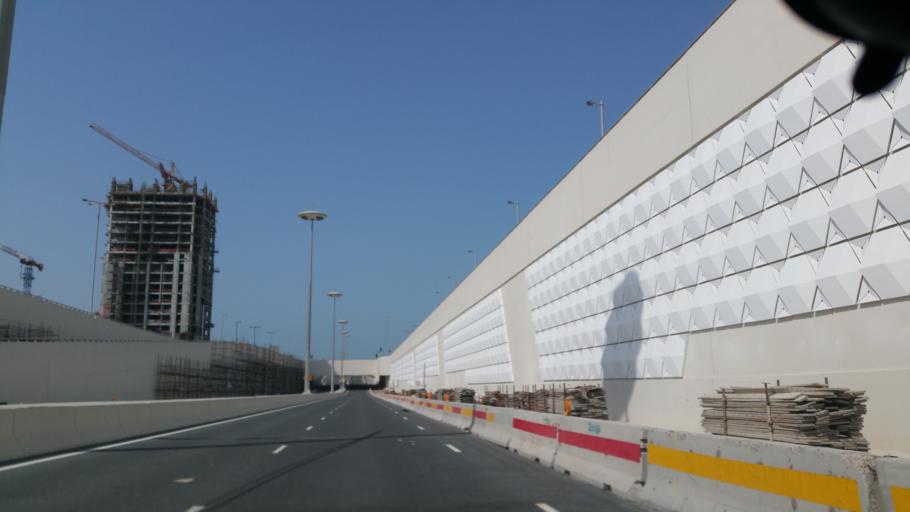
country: QA
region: Baladiyat Umm Salal
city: Umm Salal Muhammad
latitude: 25.4277
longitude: 51.5100
